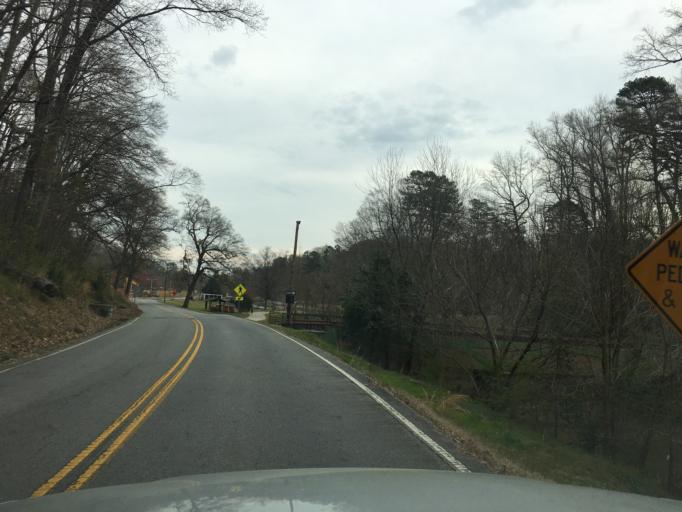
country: US
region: South Carolina
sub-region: Greenville County
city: Greenville
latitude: 34.8439
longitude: -82.3895
